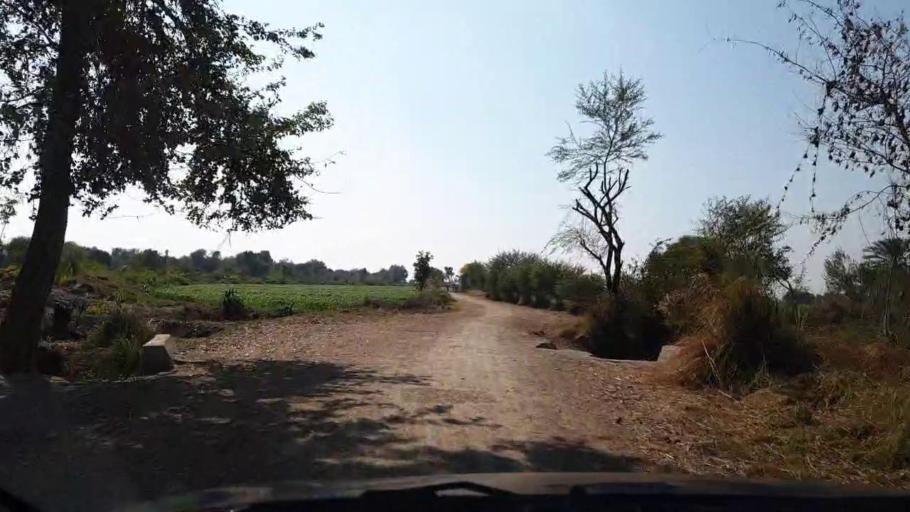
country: PK
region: Sindh
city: Sinjhoro
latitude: 25.9374
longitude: 68.7746
